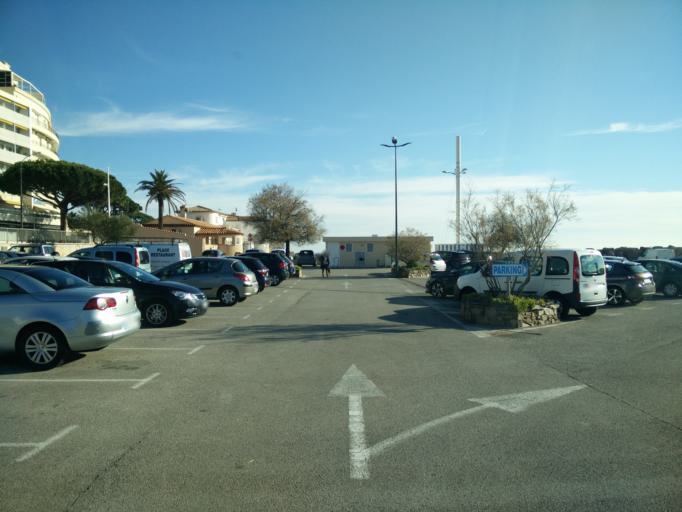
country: FR
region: Provence-Alpes-Cote d'Azur
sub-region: Departement du Var
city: Sainte-Maxime
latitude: 43.3062
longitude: 6.6419
